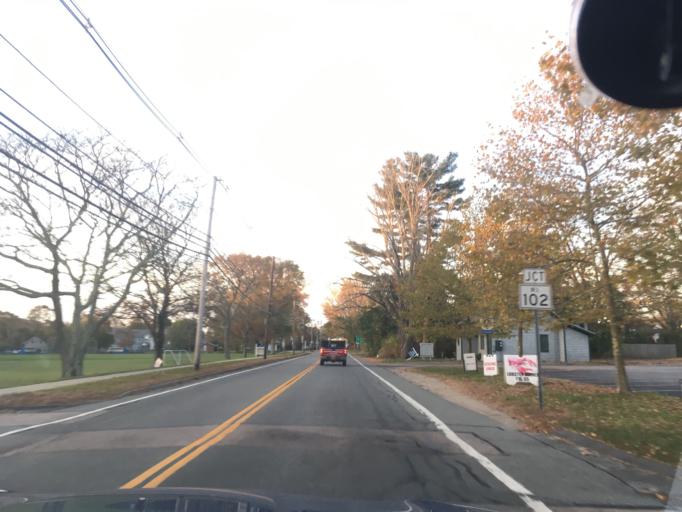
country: US
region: Rhode Island
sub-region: Washington County
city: North Kingstown
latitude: 41.5685
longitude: -71.4621
